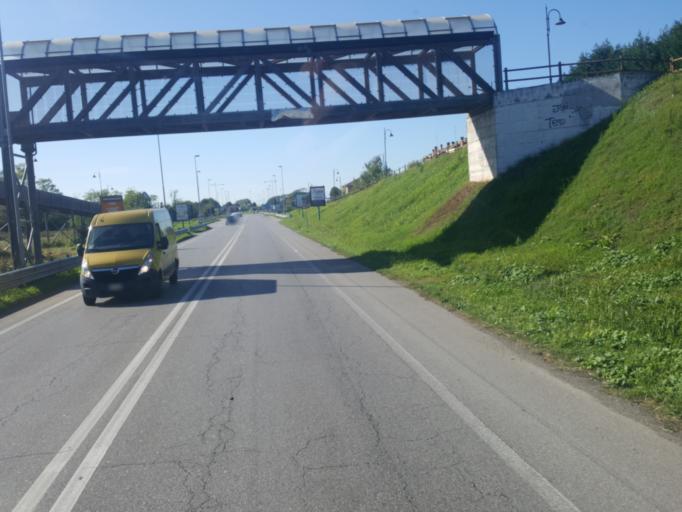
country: IT
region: Lombardy
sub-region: Citta metropolitana di Milano
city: Vittuone
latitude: 45.4820
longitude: 8.9557
